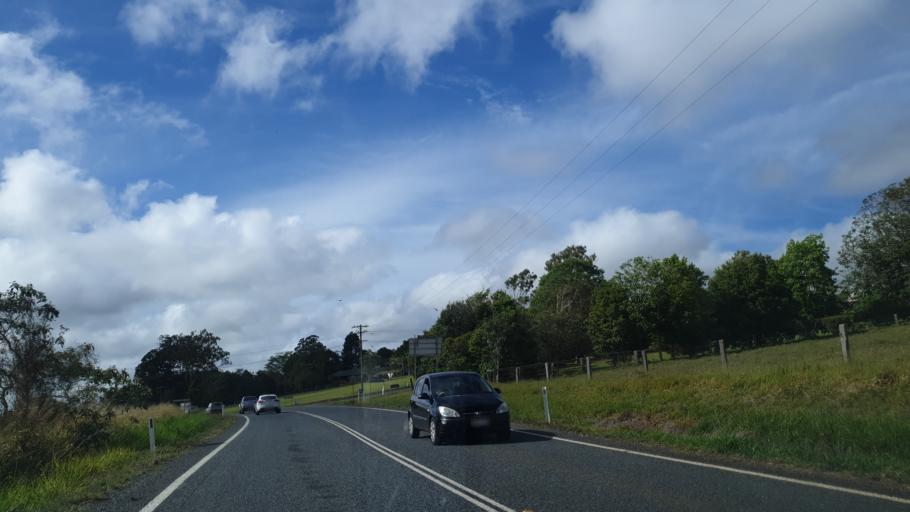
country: AU
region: Queensland
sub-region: Tablelands
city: Atherton
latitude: -17.3480
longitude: 145.5801
